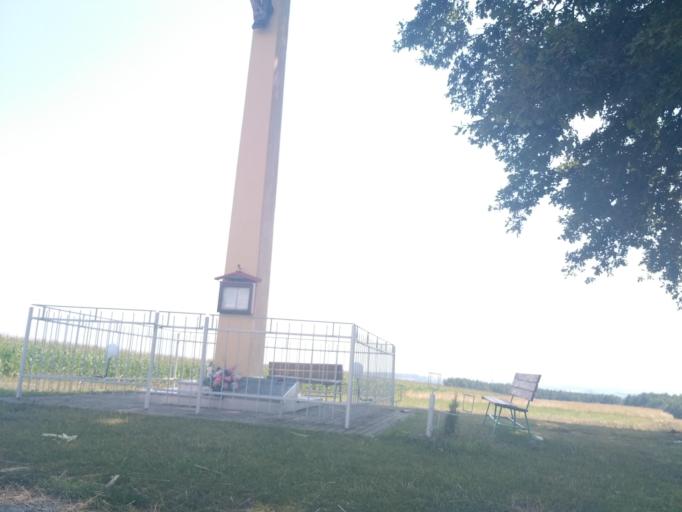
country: PL
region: Subcarpathian Voivodeship
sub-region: Powiat lancucki
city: Krzemienica
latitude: 50.0475
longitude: 22.1969
